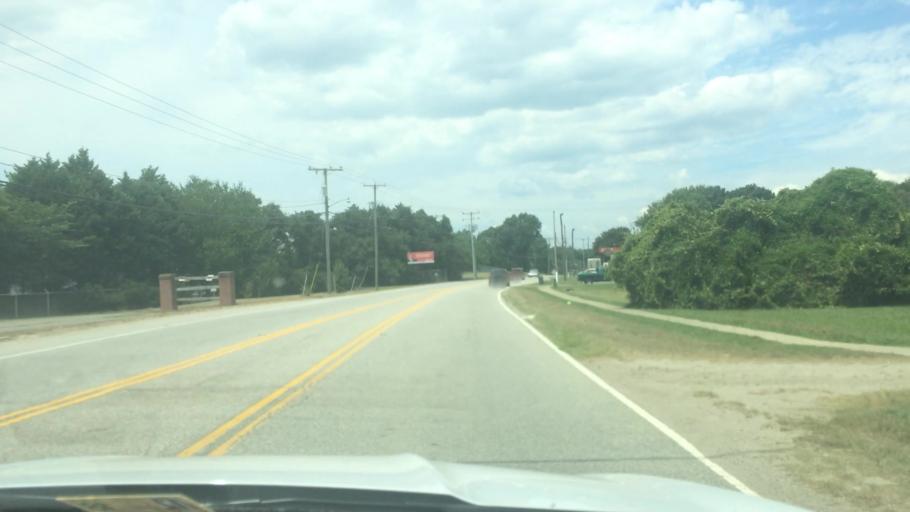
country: US
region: Virginia
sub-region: York County
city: Yorktown
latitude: 37.2072
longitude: -76.6095
